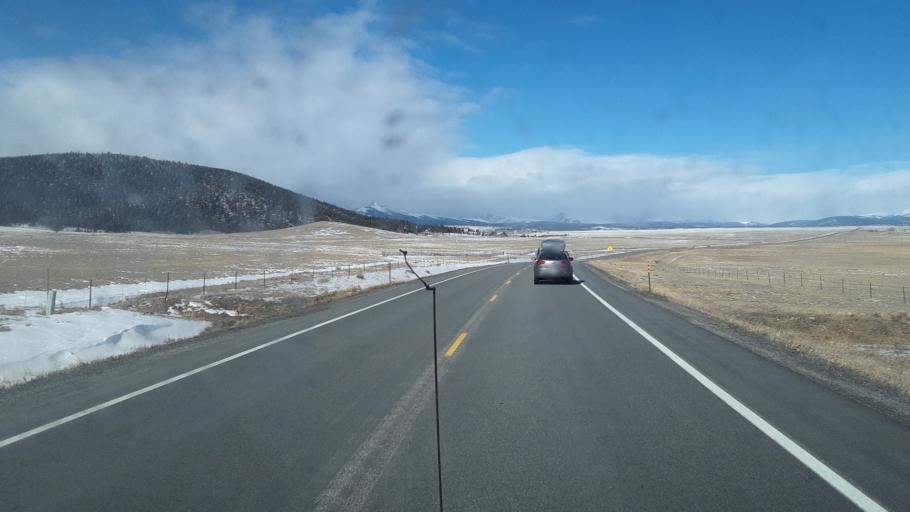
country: US
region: Colorado
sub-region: Park County
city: Fairplay
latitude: 39.0936
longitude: -105.9862
